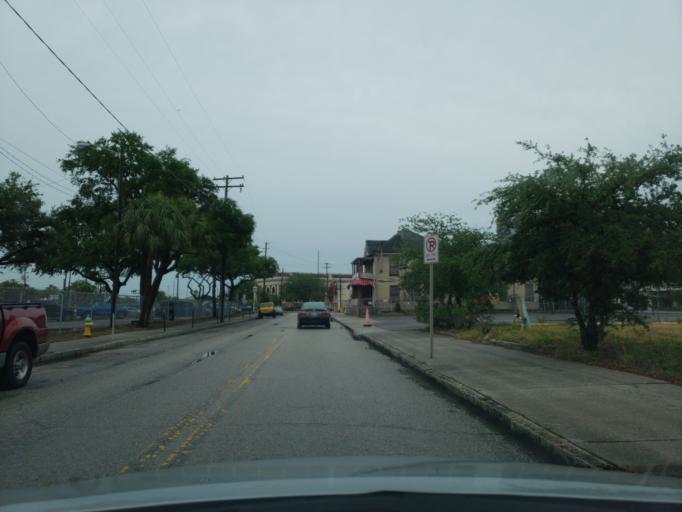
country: US
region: Florida
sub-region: Hillsborough County
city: Tampa
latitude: 27.9520
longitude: -82.4525
